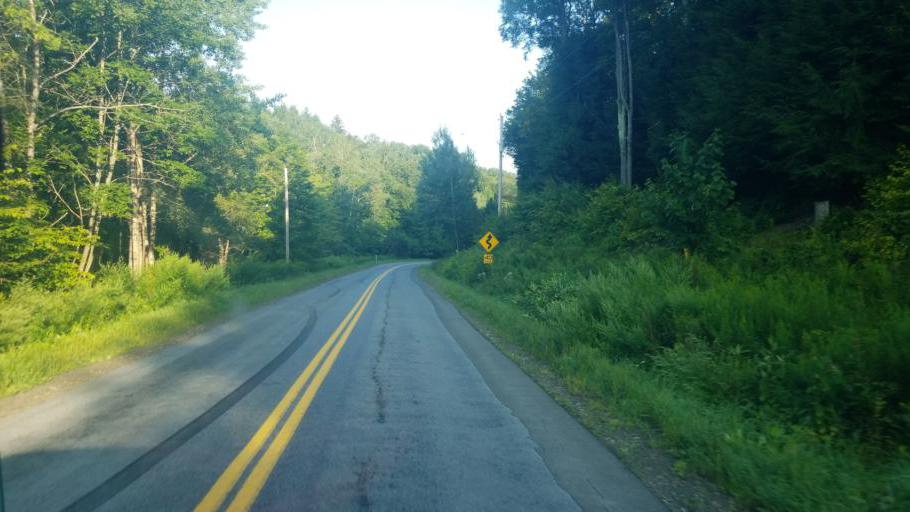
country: US
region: New York
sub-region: Allegany County
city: Andover
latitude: 42.0749
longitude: -77.6440
